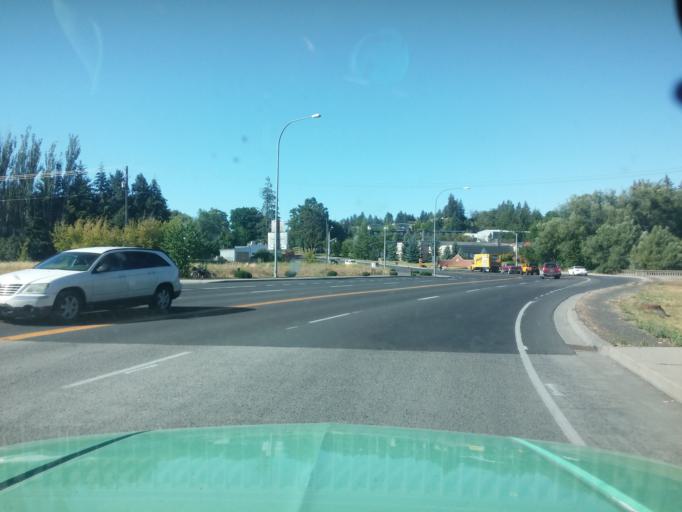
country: US
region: Idaho
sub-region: Latah County
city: Moscow
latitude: 46.7259
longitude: -117.0004
